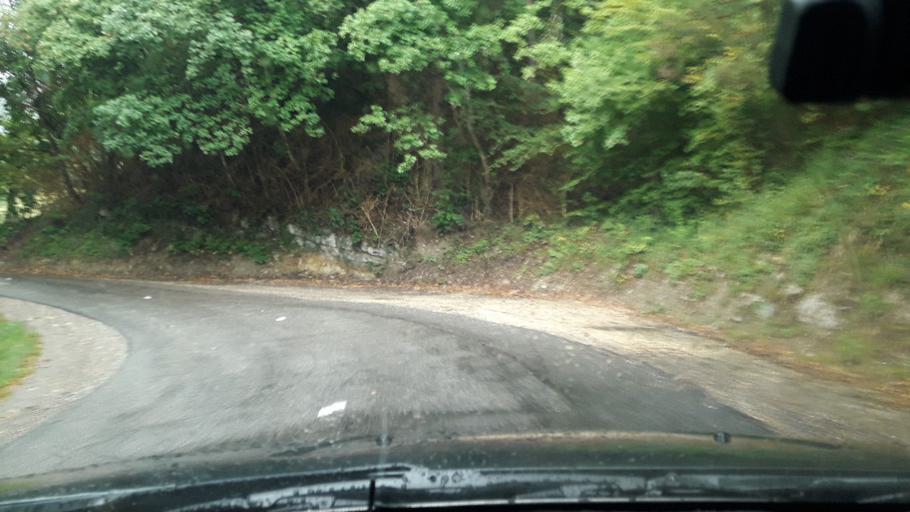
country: FR
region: Rhone-Alpes
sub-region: Departement de la Savoie
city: Saint-Baldoph
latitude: 45.5240
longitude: 5.9362
